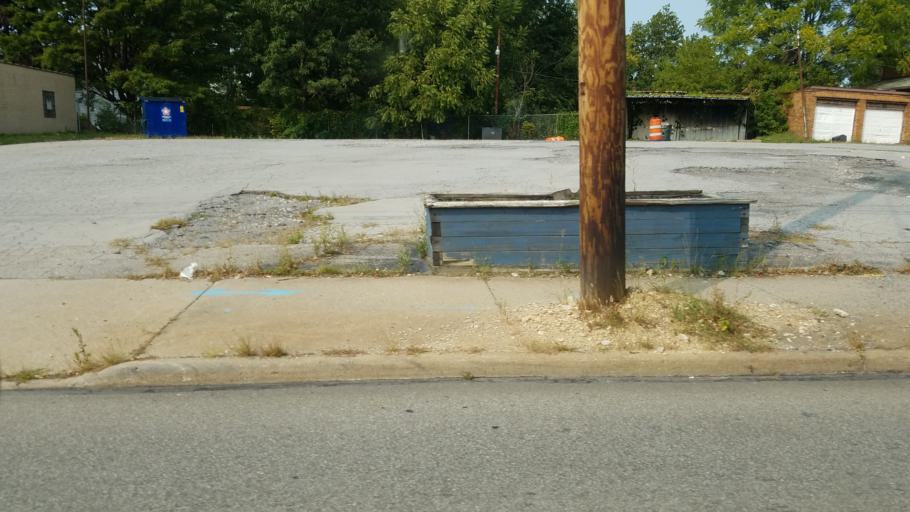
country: US
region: Ohio
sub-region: Mahoning County
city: Youngstown
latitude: 41.0707
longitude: -80.6462
